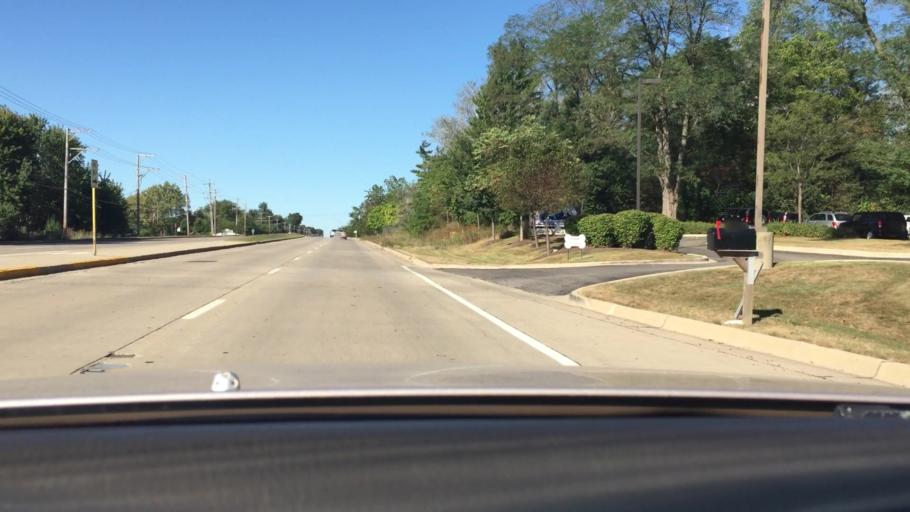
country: US
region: Illinois
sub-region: Lake County
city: Forest Lake
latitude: 42.1975
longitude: -88.0637
